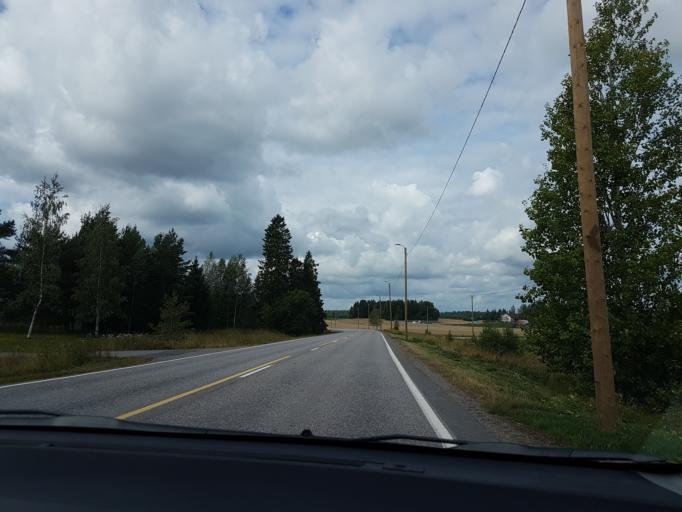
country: FI
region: Uusimaa
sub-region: Helsinki
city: Pornainen
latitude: 60.4856
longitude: 25.3563
